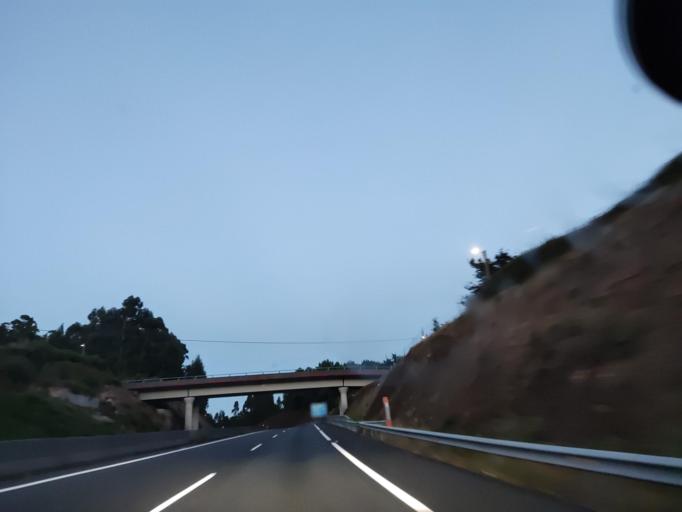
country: ES
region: Galicia
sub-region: Provincia da Coruna
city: Boiro
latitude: 42.6237
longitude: -8.9391
